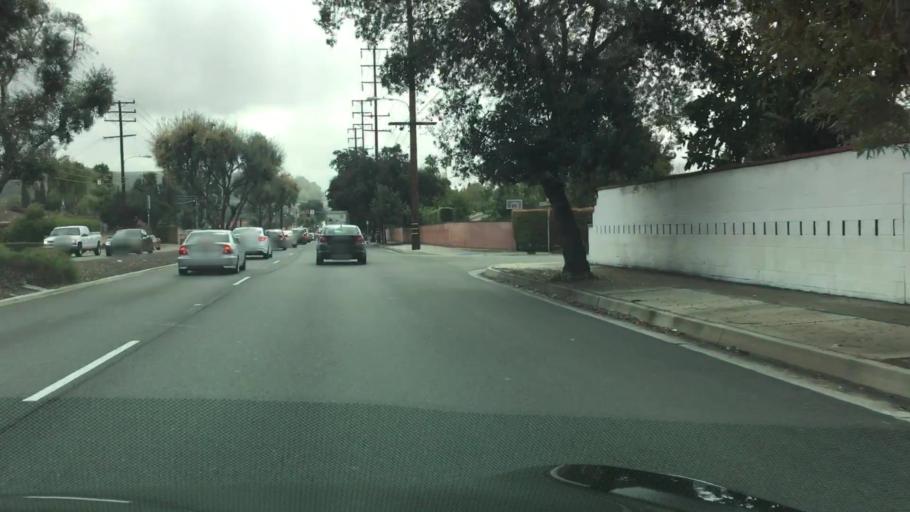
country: US
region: California
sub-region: Los Angeles County
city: West Covina
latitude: 34.0556
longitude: -117.9081
